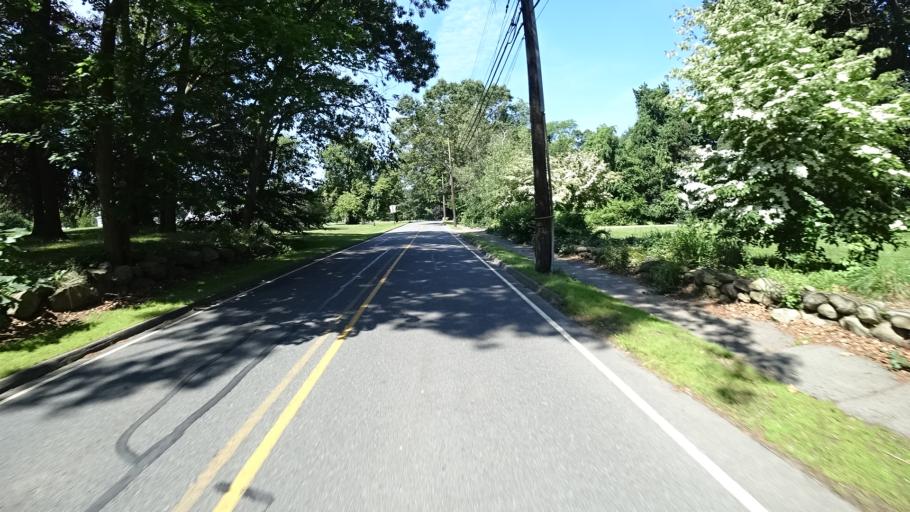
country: US
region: Massachusetts
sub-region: Norfolk County
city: Dedham
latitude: 42.2410
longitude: -71.1626
